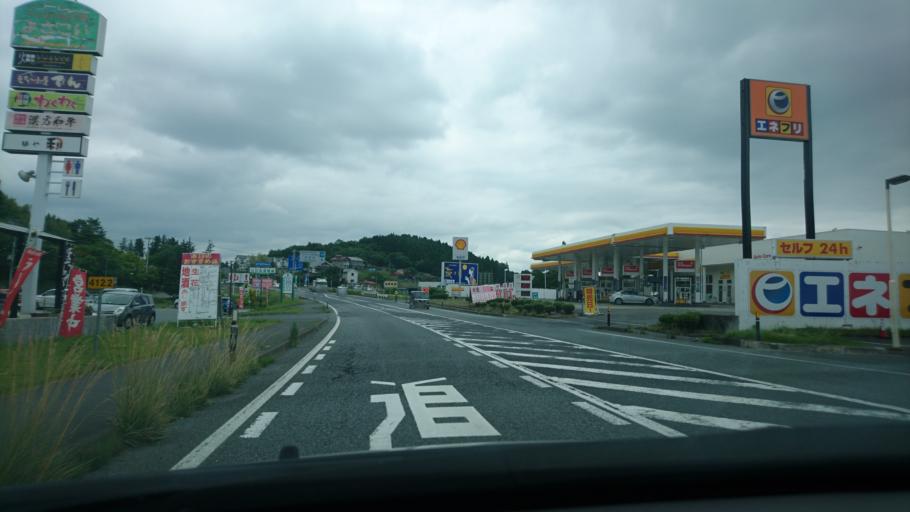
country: JP
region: Miyagi
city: Furukawa
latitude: 38.7121
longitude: 141.0195
